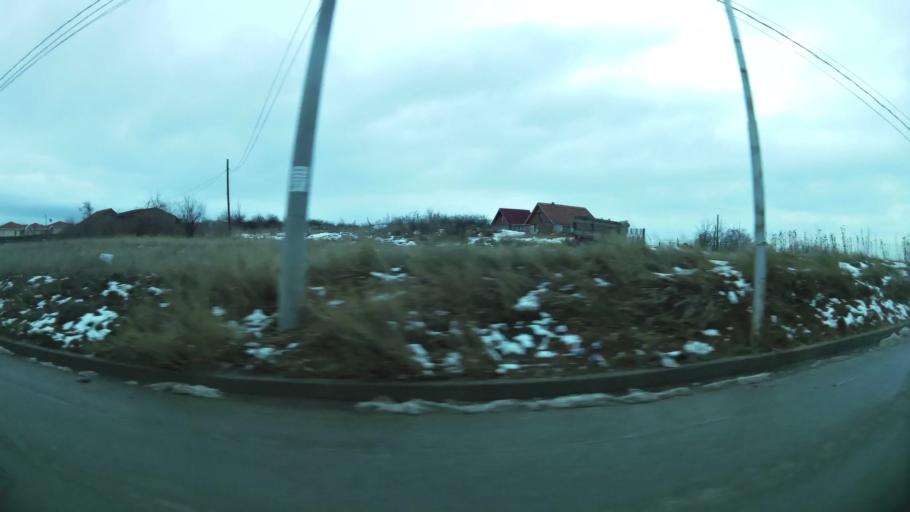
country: XK
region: Pristina
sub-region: Komuna e Prishtines
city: Pristina
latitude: 42.6325
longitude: 21.1682
